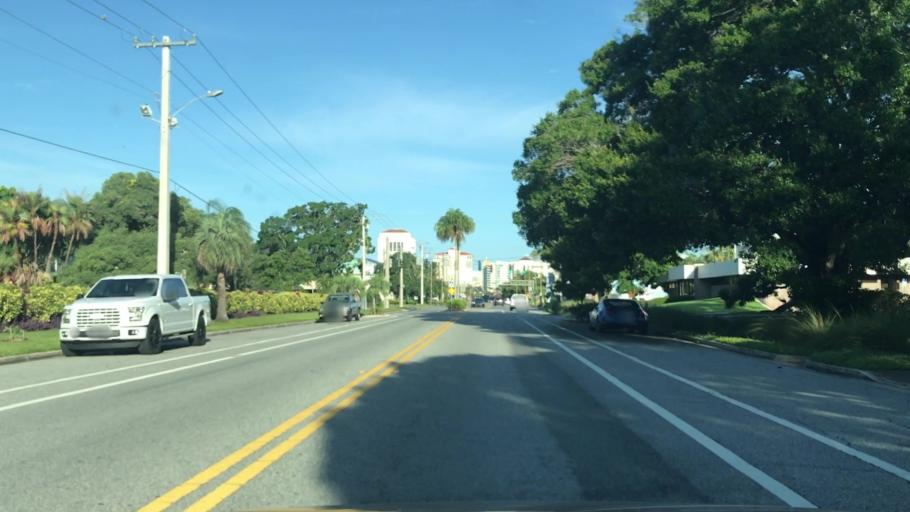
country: US
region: Florida
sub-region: Sarasota County
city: Sarasota
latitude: 27.3356
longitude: -82.5230
